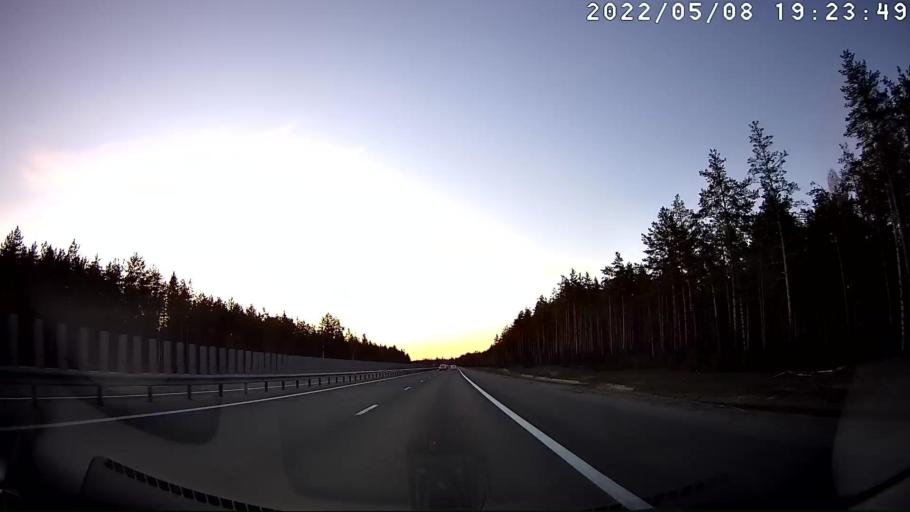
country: RU
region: Mariy-El
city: Surok
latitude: 56.4183
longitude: 48.1440
